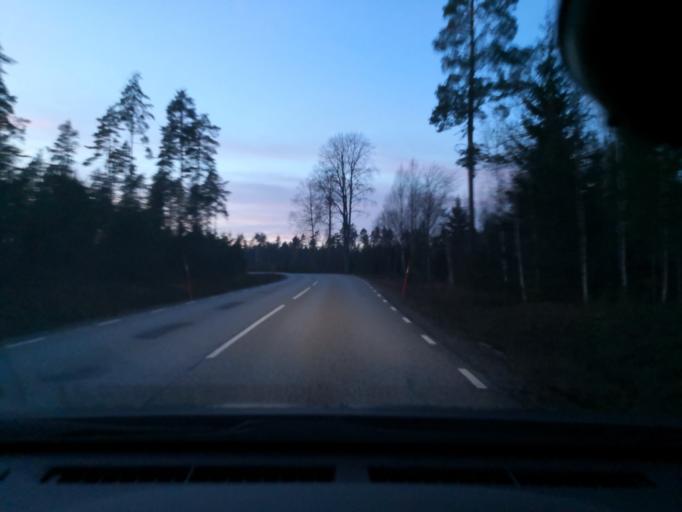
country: SE
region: OErebro
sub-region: Lindesbergs Kommun
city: Fellingsbro
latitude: 59.4034
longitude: 15.5022
